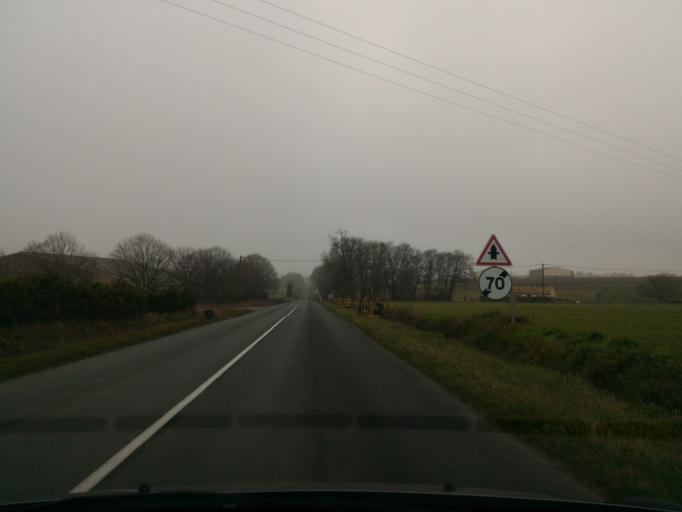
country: FR
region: Poitou-Charentes
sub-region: Departement de la Charente
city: Rouillac
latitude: 45.7689
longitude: -0.0828
